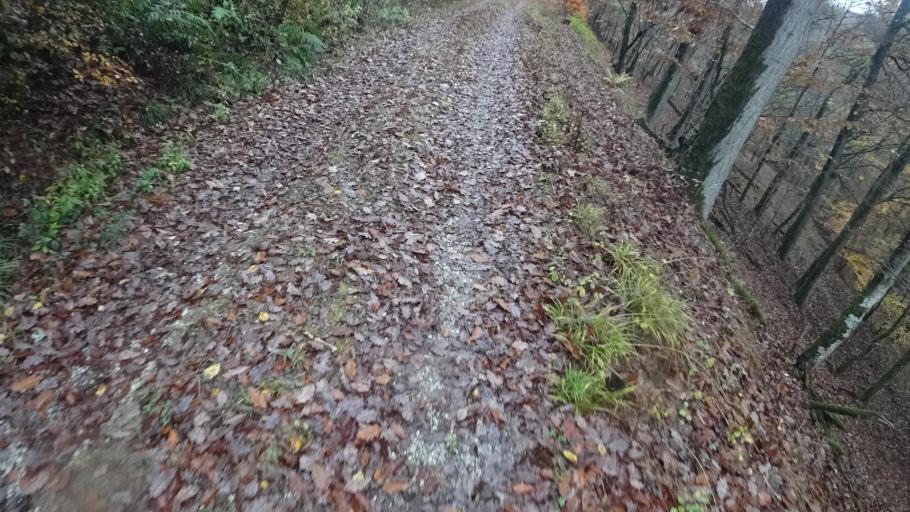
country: DE
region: Rheinland-Pfalz
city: Utzenhain
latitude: 50.1460
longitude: 7.6558
